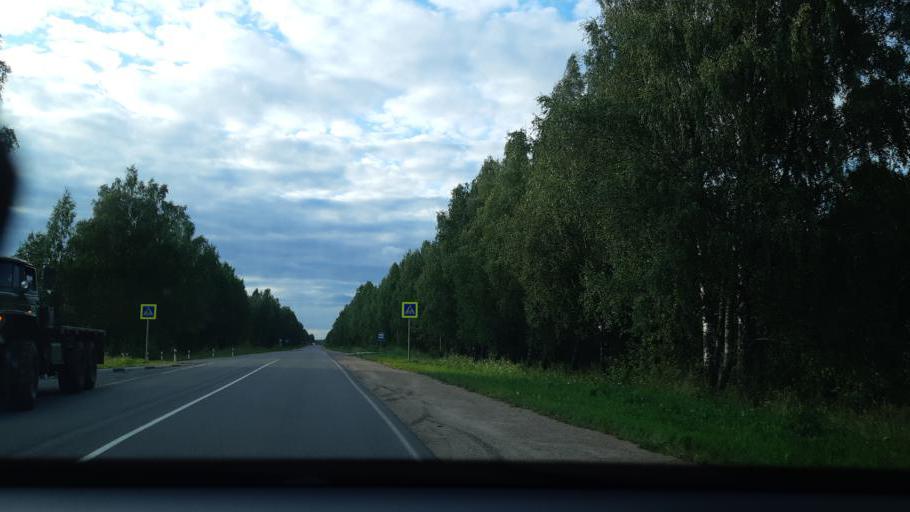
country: RU
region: Smolensk
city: Yel'nya
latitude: 54.5953
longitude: 33.1892
